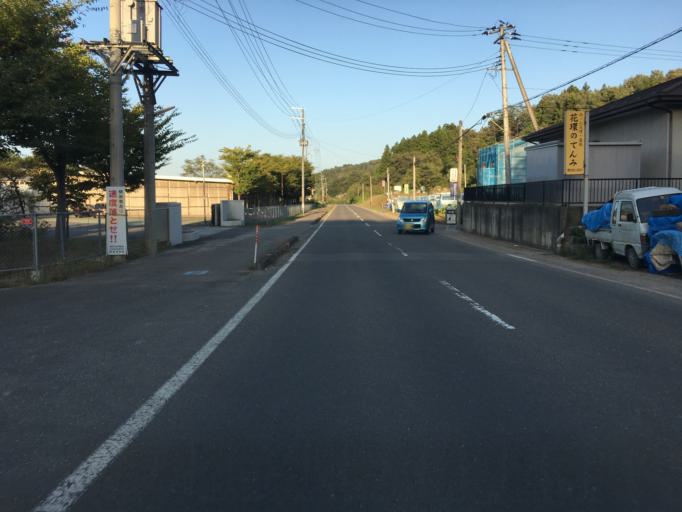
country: JP
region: Fukushima
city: Hobaramachi
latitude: 37.7864
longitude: 140.5237
